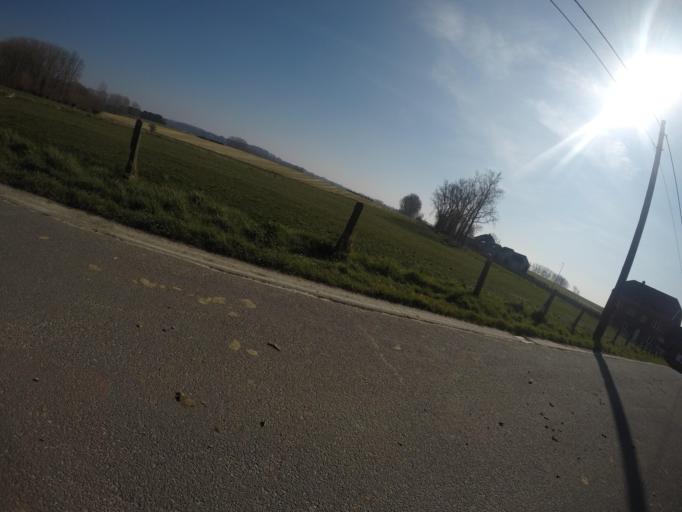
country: BE
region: Flanders
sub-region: Provincie Oost-Vlaanderen
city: Geraardsbergen
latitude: 50.7829
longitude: 3.8531
